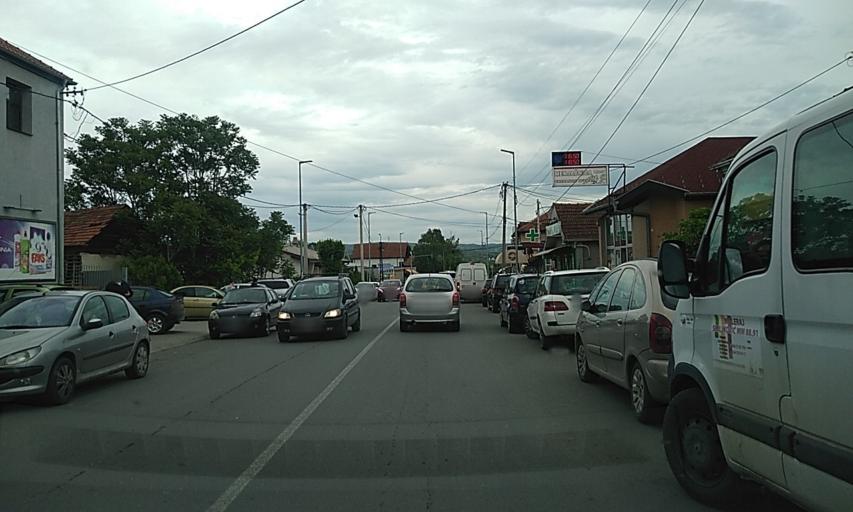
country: RS
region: Central Serbia
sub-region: Rasinski Okrug
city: Krusevac
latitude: 43.5861
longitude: 21.3388
